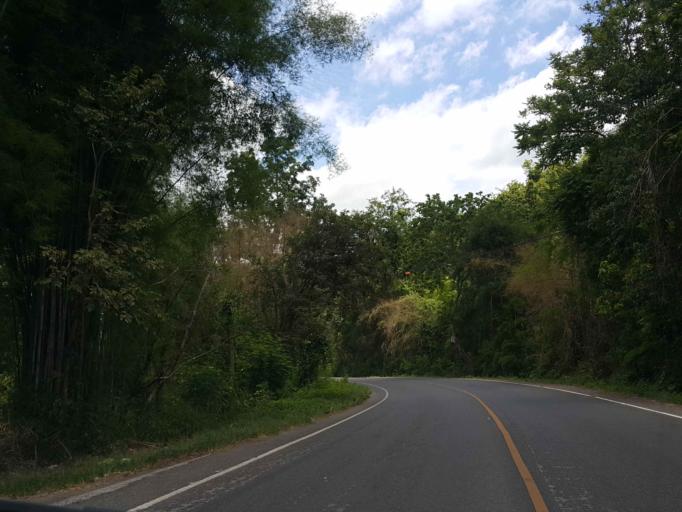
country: TH
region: Chiang Mai
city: Hang Dong
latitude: 18.7597
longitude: 98.8790
